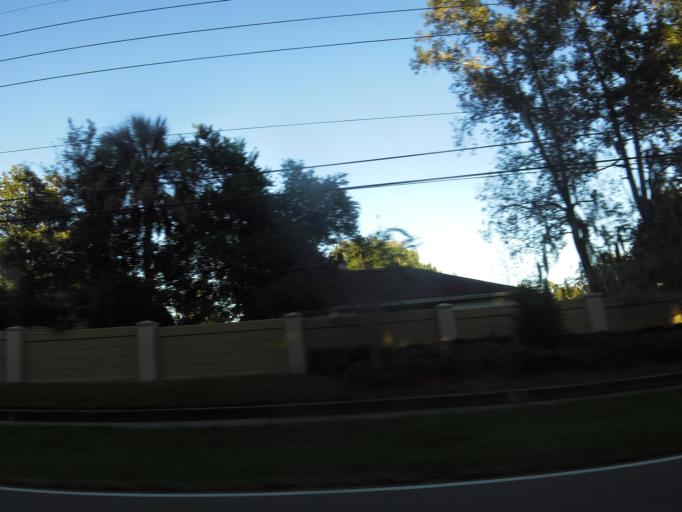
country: US
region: Florida
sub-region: Duval County
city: Neptune Beach
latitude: 30.3083
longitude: -81.4458
